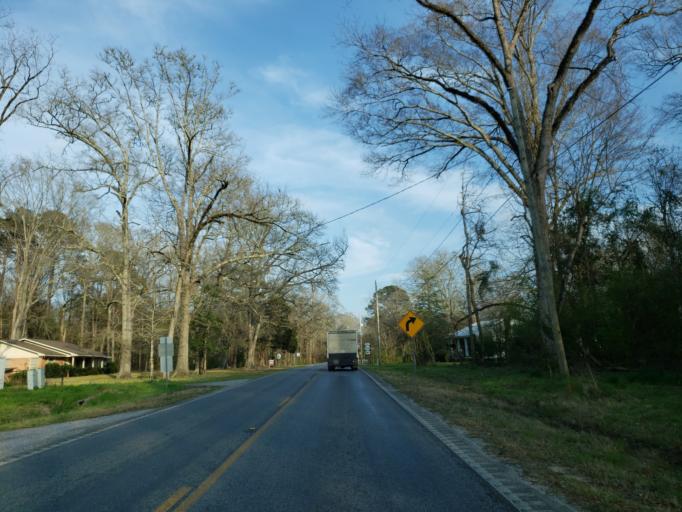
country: US
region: Mississippi
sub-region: Clarke County
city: Stonewall
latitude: 32.1759
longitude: -88.8123
